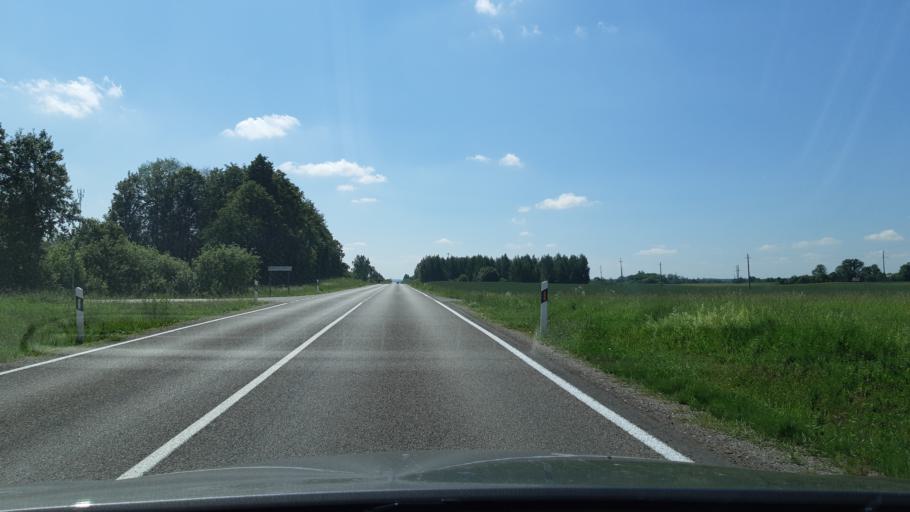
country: LT
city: Jieznas
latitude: 54.5930
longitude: 24.1644
